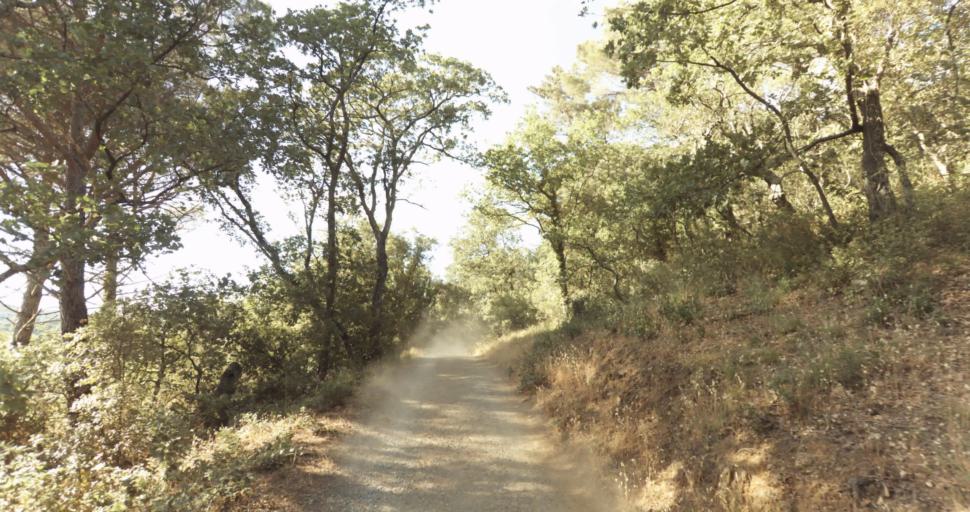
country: FR
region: Provence-Alpes-Cote d'Azur
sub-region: Departement du Var
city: Gassin
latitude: 43.2268
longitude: 6.5800
